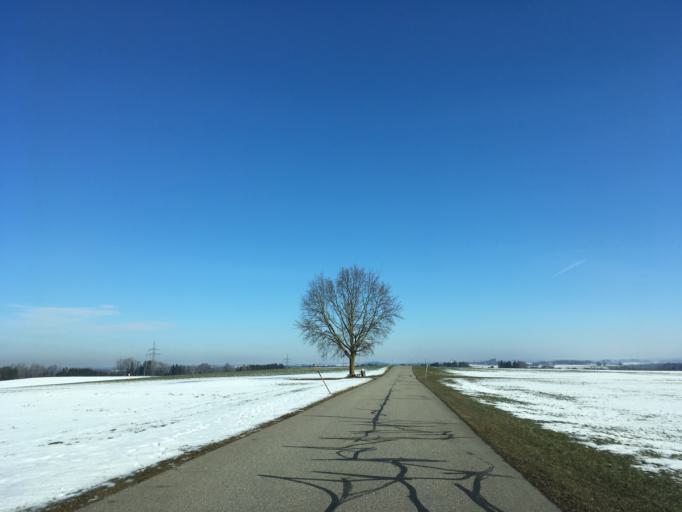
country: DE
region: Bavaria
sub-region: Upper Bavaria
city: Schechen
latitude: 47.9229
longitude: 12.1571
